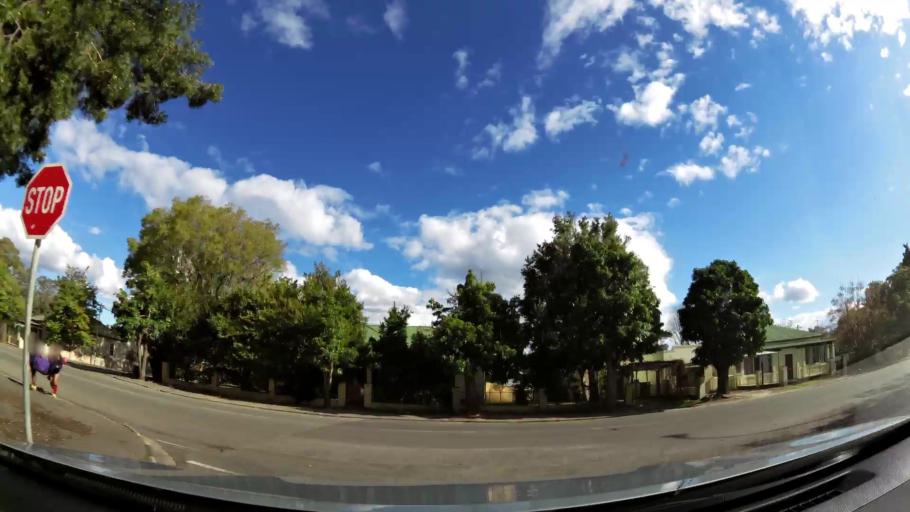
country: ZA
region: Western Cape
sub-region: Overberg District Municipality
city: Swellendam
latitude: -34.0251
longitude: 20.4414
